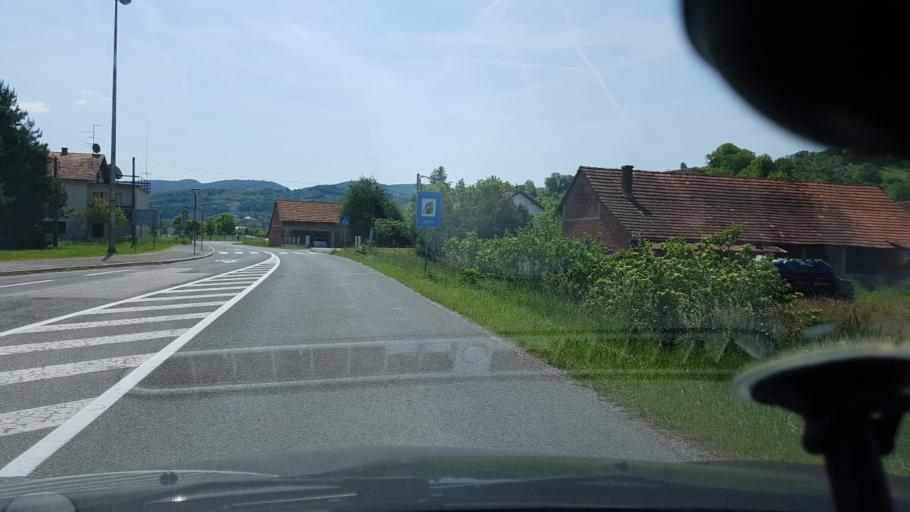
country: HR
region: Krapinsko-Zagorska
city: Marija Bistrica
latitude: 46.0051
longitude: 16.1093
